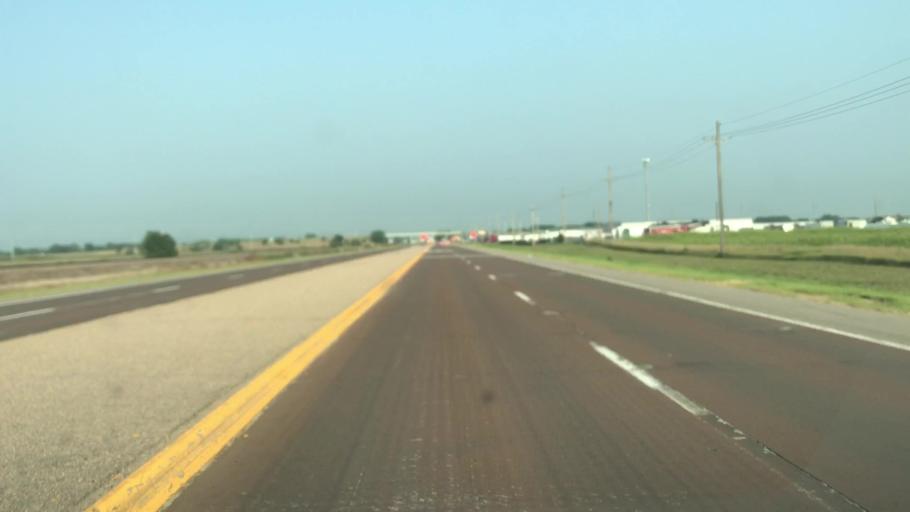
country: US
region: Nebraska
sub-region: Hall County
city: Grand Island
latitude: 40.9560
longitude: -98.3956
